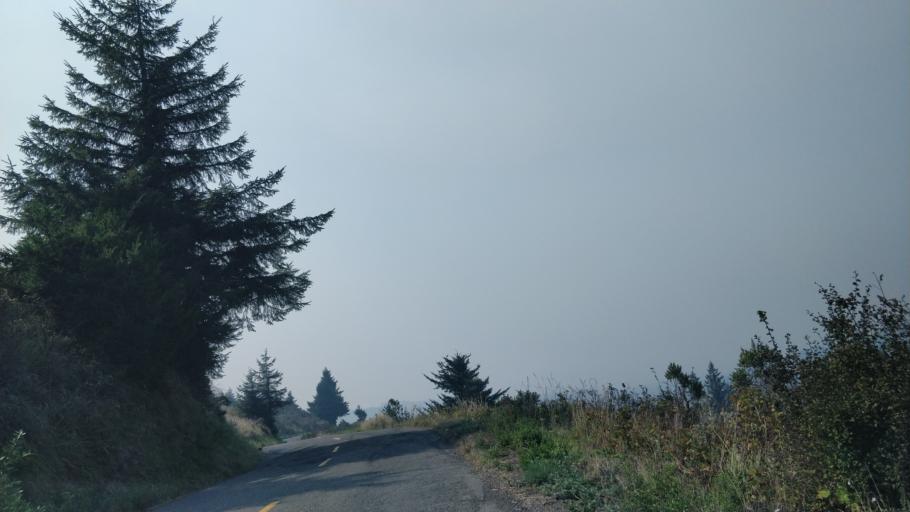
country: US
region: California
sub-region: Humboldt County
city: Ferndale
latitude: 40.5055
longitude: -124.3023
